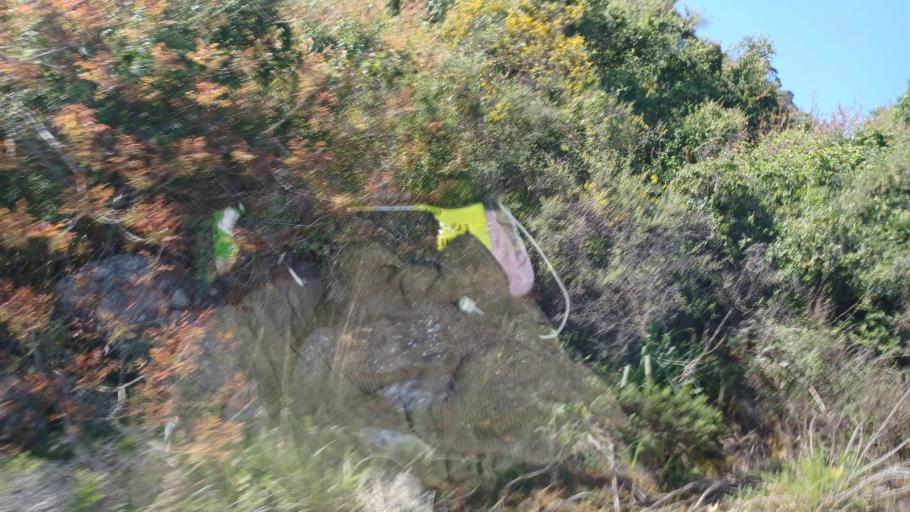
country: CY
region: Pafos
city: Polis
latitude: 34.9702
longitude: 32.3951
